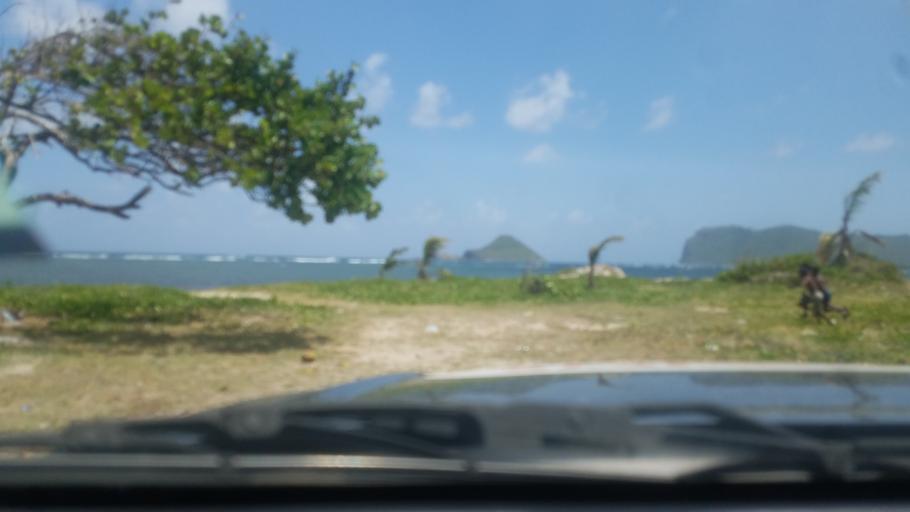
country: LC
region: Vieux-Fort
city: Vieux Fort
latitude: 13.7478
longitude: -60.9330
